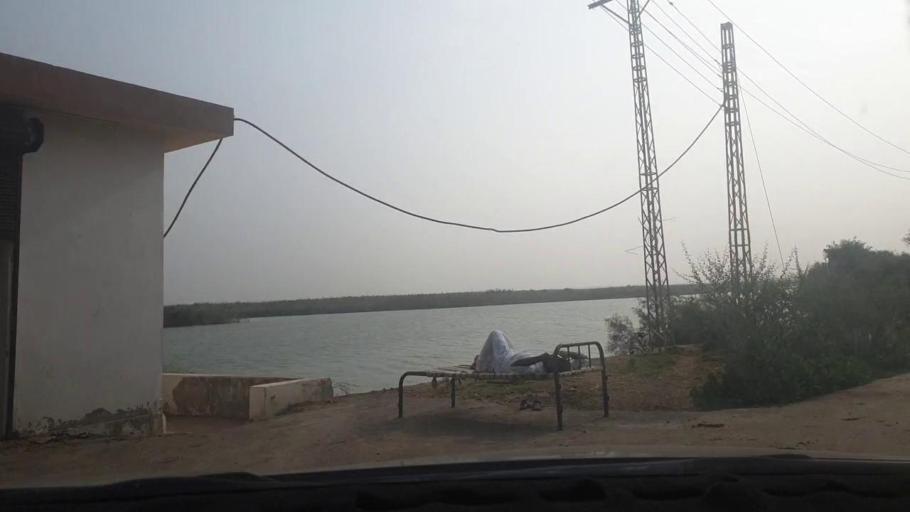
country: PK
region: Sindh
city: Jamshoro
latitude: 25.5046
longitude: 68.3175
